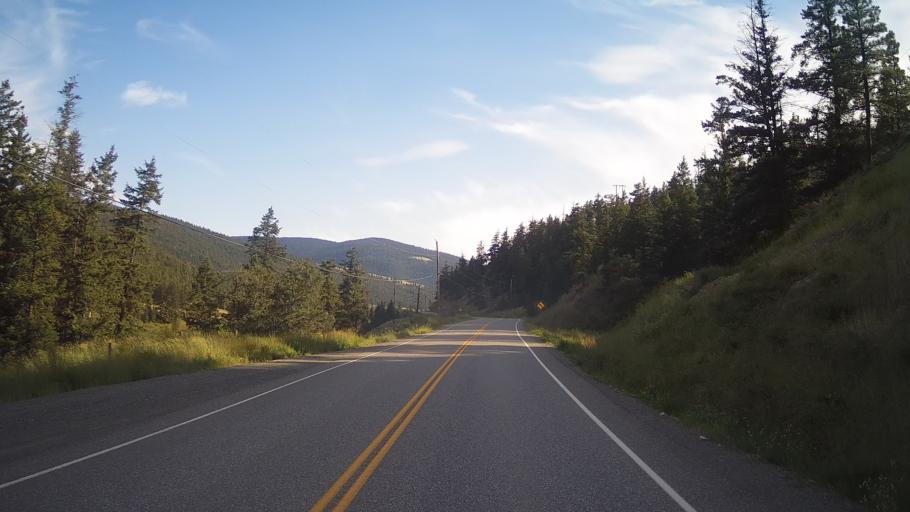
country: CA
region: British Columbia
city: Cache Creek
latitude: 50.8608
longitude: -121.5296
